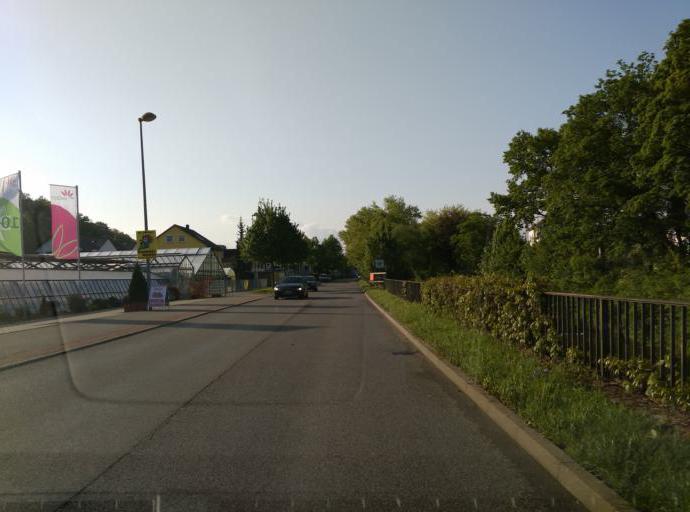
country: DE
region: Baden-Wuerttemberg
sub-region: Tuebingen Region
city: Wannweil
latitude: 48.5202
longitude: 9.1470
